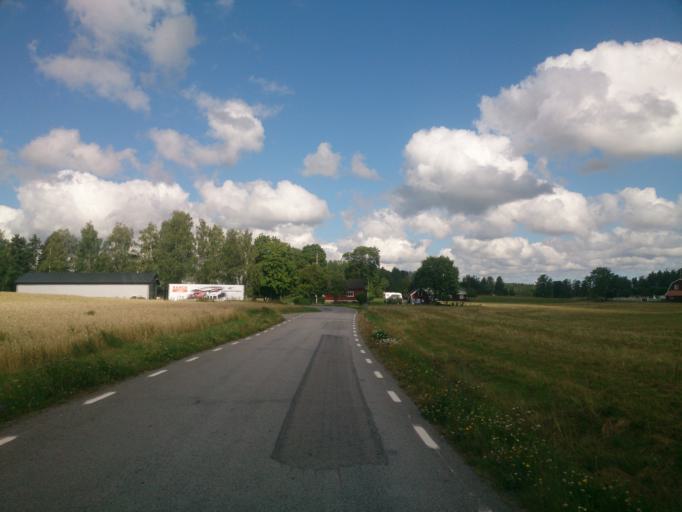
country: SE
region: OEstergoetland
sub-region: Atvidabergs Kommun
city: Atvidaberg
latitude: 58.3207
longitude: 15.9221
